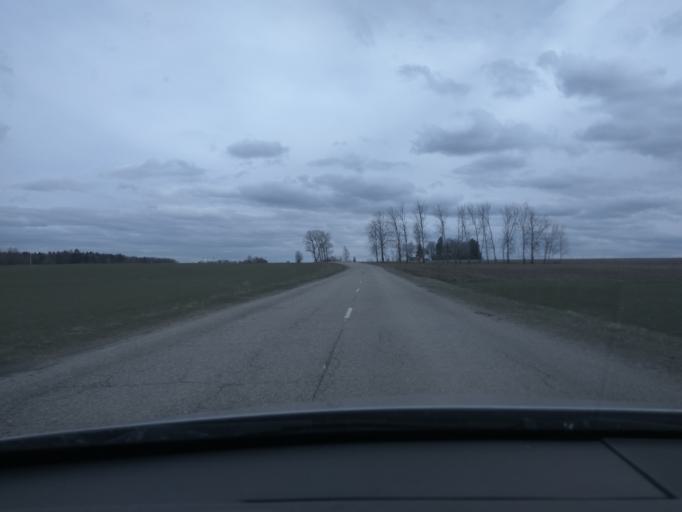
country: LV
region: Aizpute
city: Aizpute
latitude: 56.7577
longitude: 21.5484
